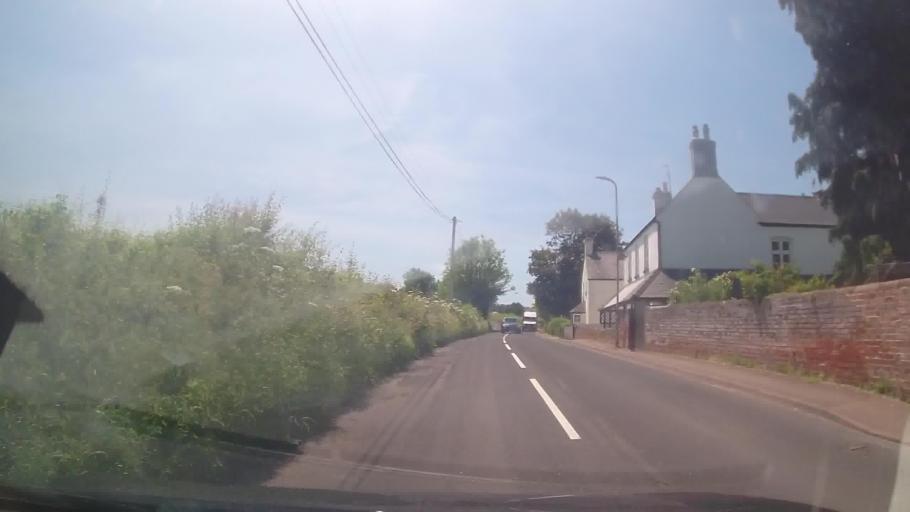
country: GB
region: Wales
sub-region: Monmouthshire
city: Monmouth
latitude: 51.8303
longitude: -2.7144
